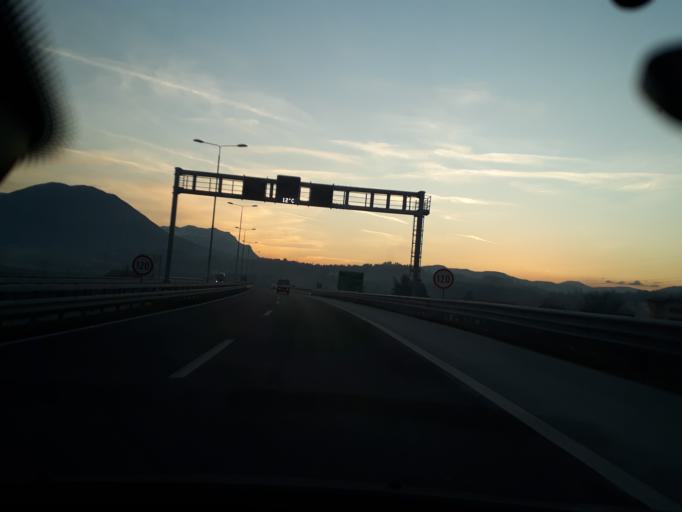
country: BA
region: Federation of Bosnia and Herzegovina
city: Vogosca
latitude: 43.8707
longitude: 18.2847
